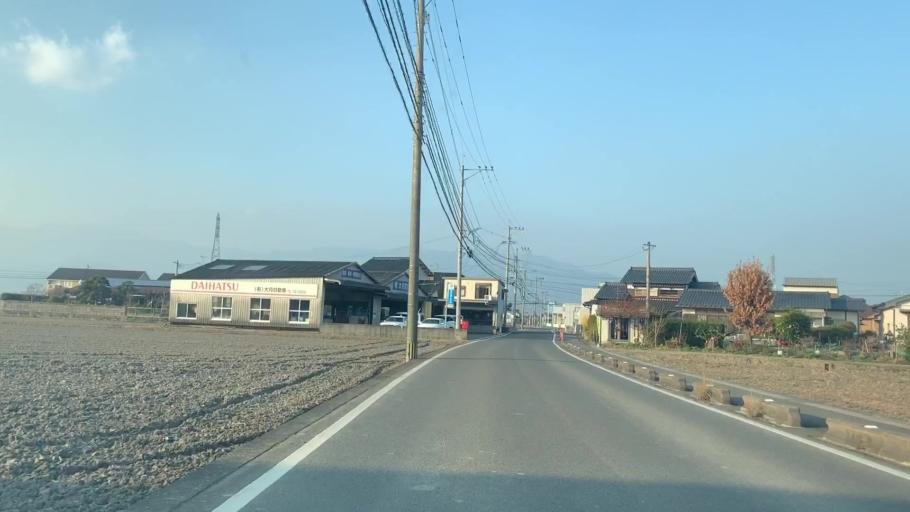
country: JP
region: Saga Prefecture
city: Saga-shi
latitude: 33.2651
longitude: 130.2309
